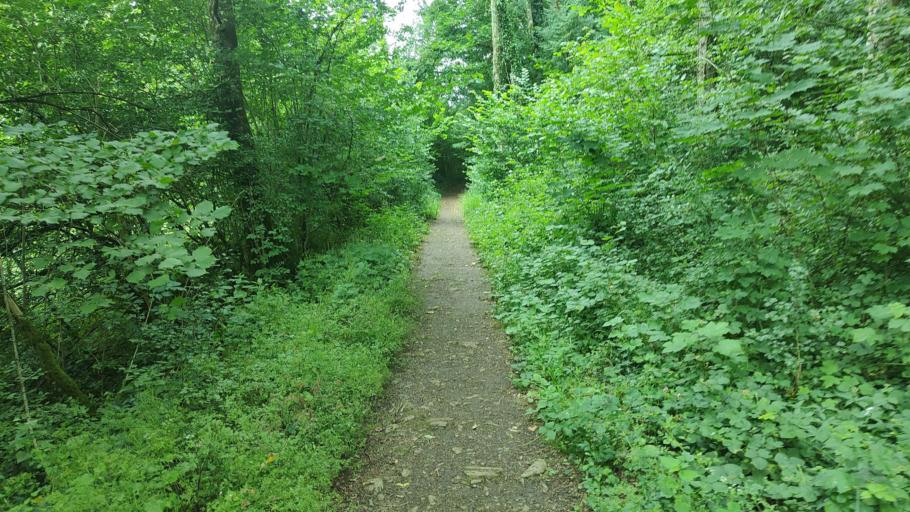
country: BE
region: Wallonia
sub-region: Province du Hainaut
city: Chimay
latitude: 50.0606
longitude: 4.3674
